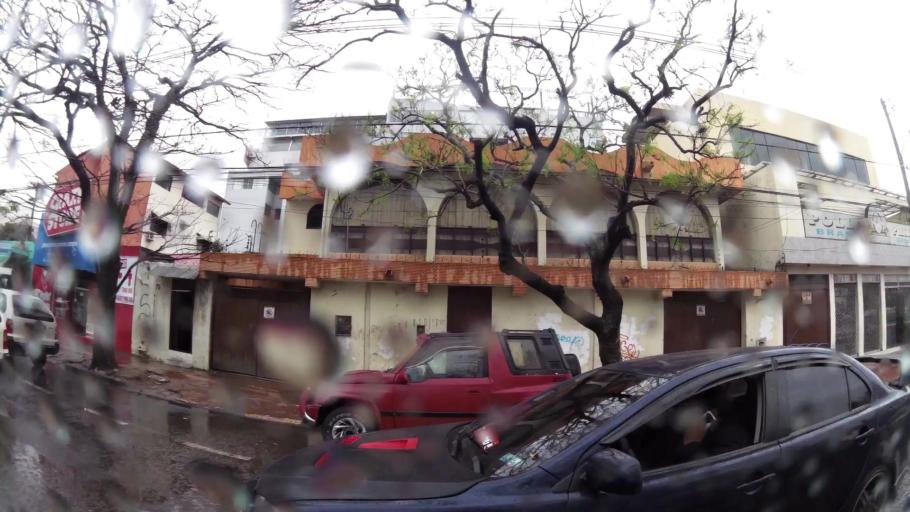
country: BO
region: Santa Cruz
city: Santa Cruz de la Sierra
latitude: -17.7837
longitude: -63.1722
